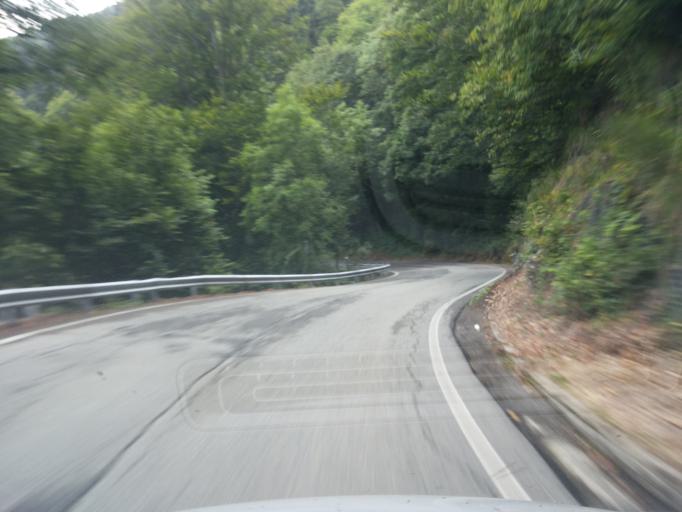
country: IT
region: Piedmont
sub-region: Provincia di Biella
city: San Paolo Cervo
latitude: 45.6180
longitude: 7.9825
